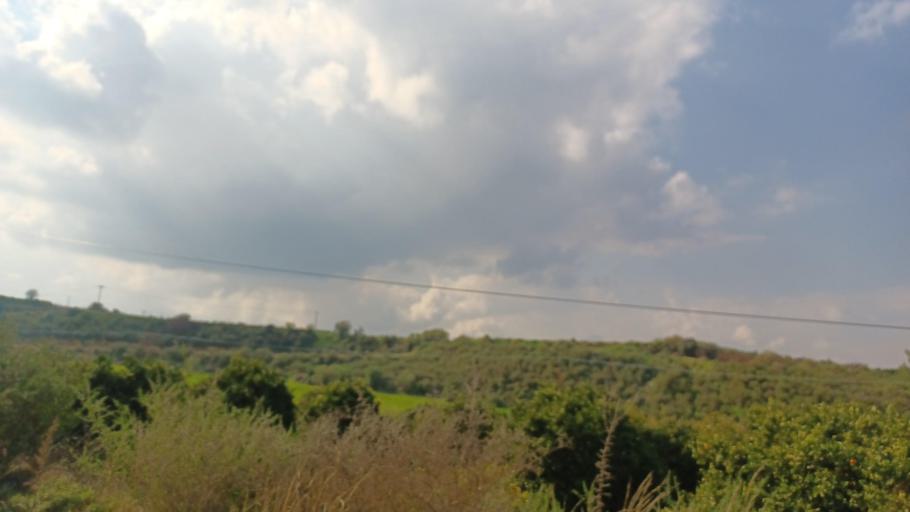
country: CY
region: Pafos
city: Polis
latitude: 35.0463
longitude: 32.4611
